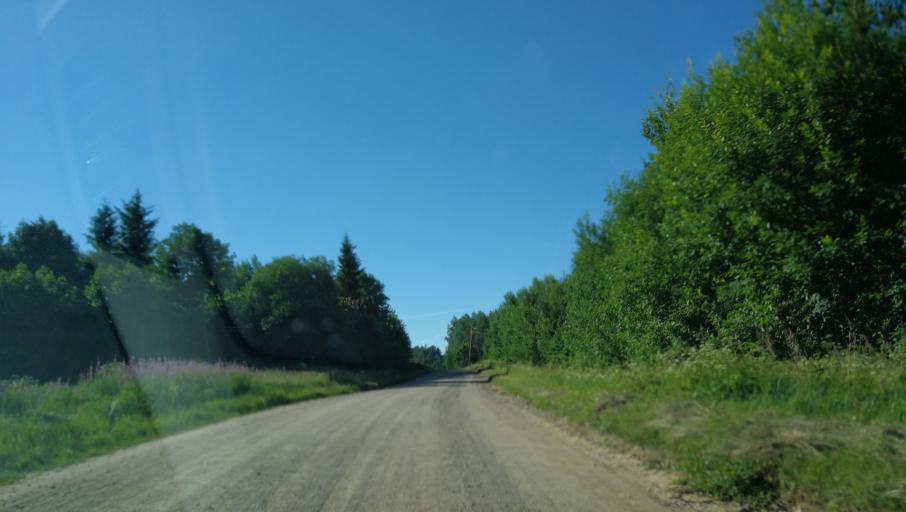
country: LV
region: Jaunpiebalga
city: Jaunpiebalga
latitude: 57.0232
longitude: 26.0321
